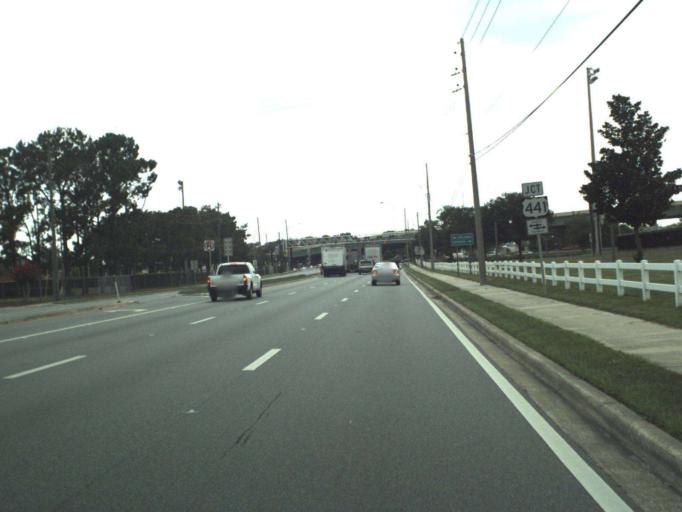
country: US
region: Florida
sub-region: Orange County
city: Fairview Shores
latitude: 28.5993
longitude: -81.4143
